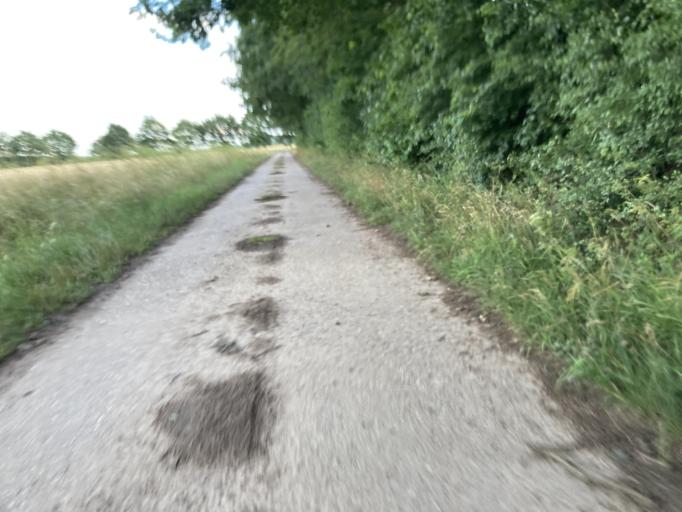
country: DE
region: Lower Saxony
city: Verden
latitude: 52.9149
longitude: 9.1942
